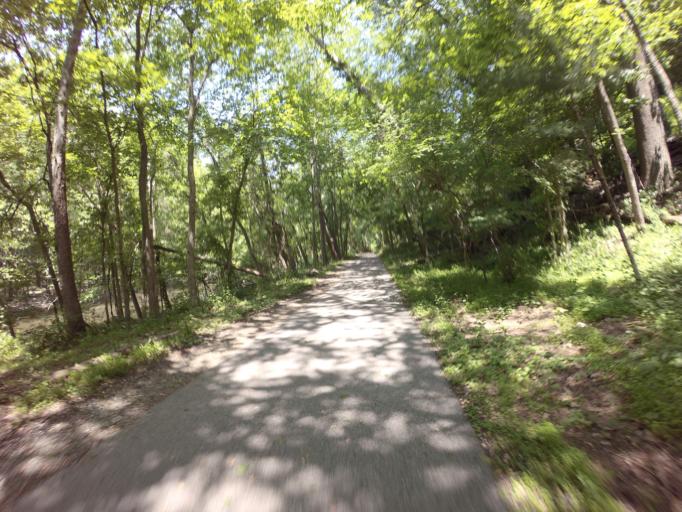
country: US
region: Maryland
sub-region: Howard County
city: Ilchester
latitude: 39.2396
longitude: -76.7470
